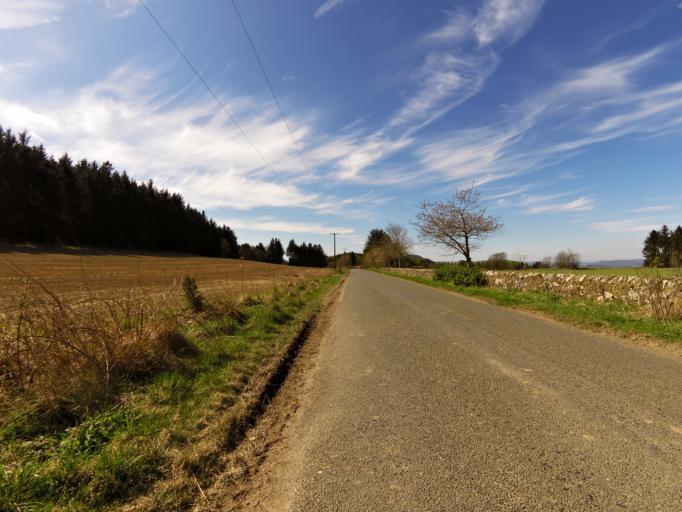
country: GB
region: Scotland
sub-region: Fife
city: Cupar
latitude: 56.3889
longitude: -3.0687
